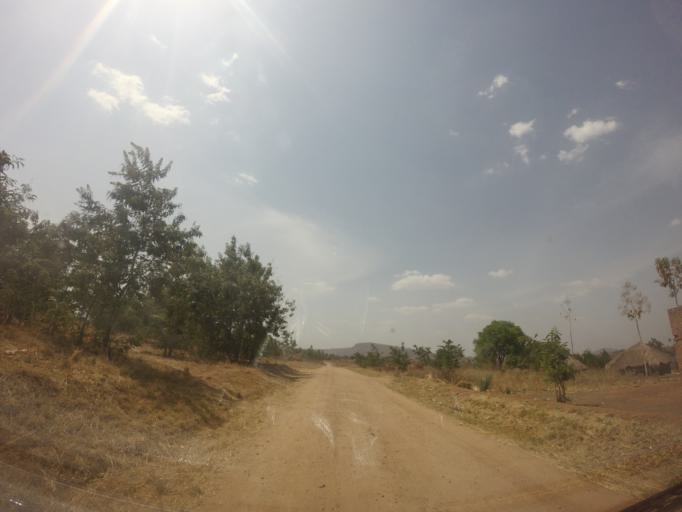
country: UG
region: Northern Region
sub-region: Arua District
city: Arua
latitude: 2.9100
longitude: 31.0524
